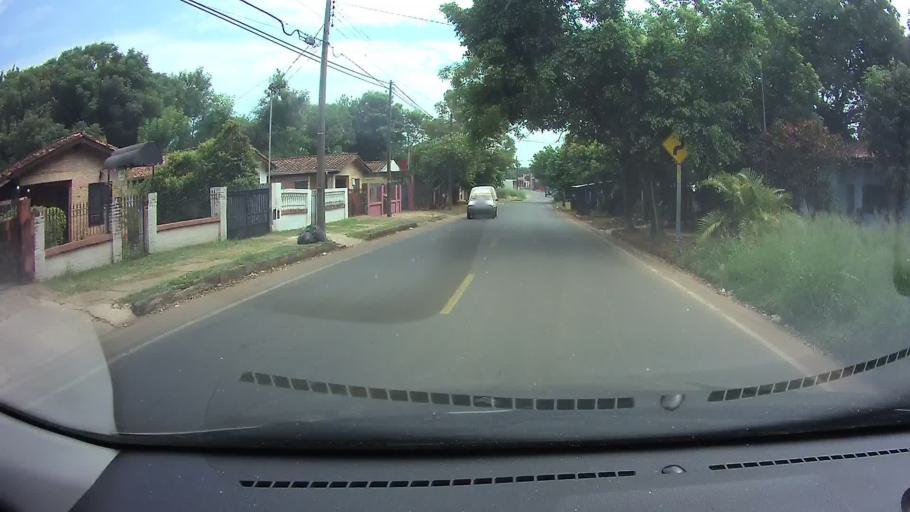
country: PY
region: Central
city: San Lorenzo
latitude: -25.2914
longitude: -57.5050
